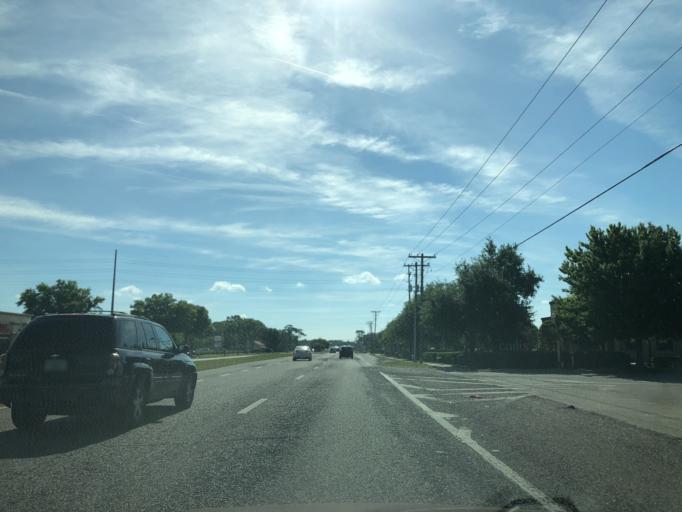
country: US
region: Florida
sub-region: Orange County
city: Apopka
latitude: 28.6877
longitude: -81.5398
